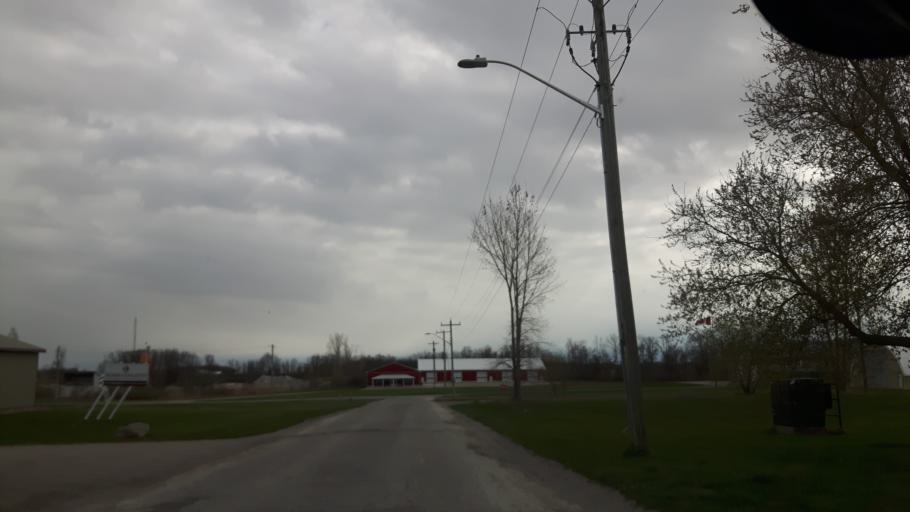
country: CA
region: Ontario
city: Bluewater
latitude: 43.6119
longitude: -81.5439
